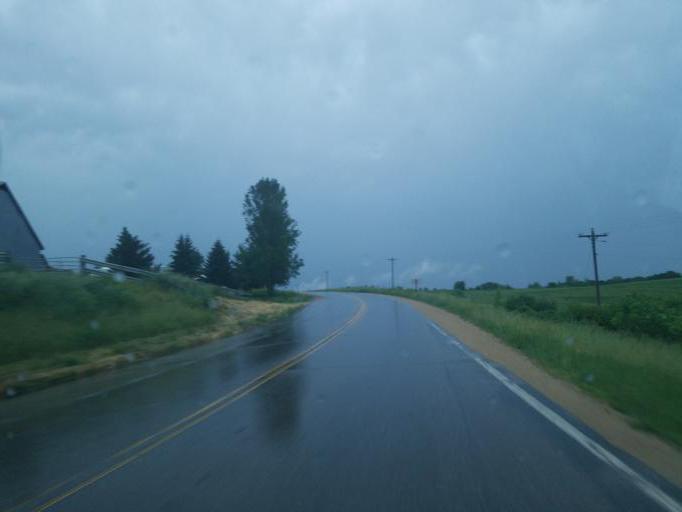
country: US
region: Wisconsin
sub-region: Vernon County
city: Hillsboro
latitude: 43.6325
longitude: -90.4523
